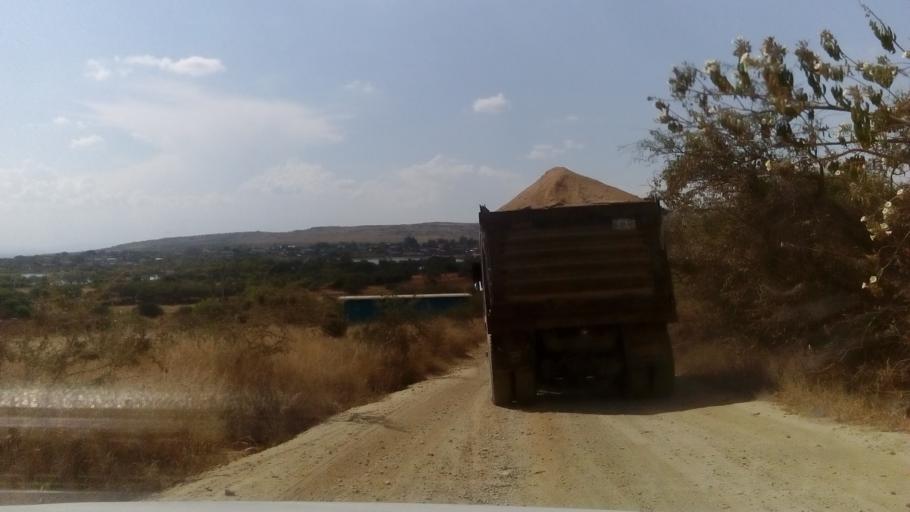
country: MX
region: Guanajuato
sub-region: Silao de la Victoria
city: Loma de Yerbabuena
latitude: 21.0684
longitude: -101.4588
